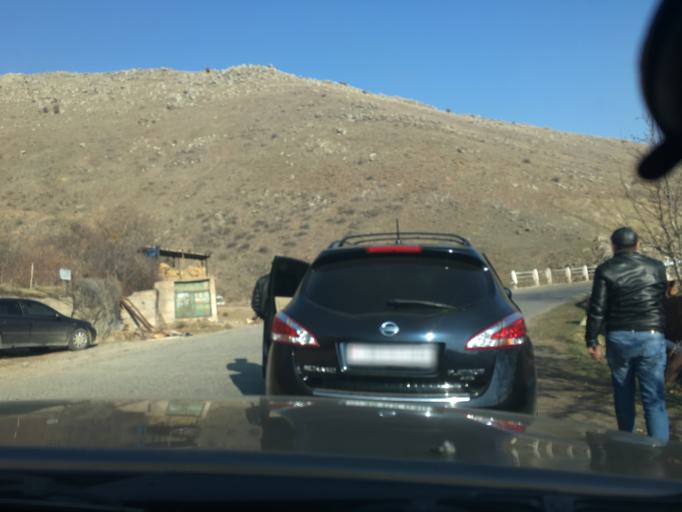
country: AM
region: Kotayk'i Marz
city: Bjni
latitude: 40.4454
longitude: 44.6314
